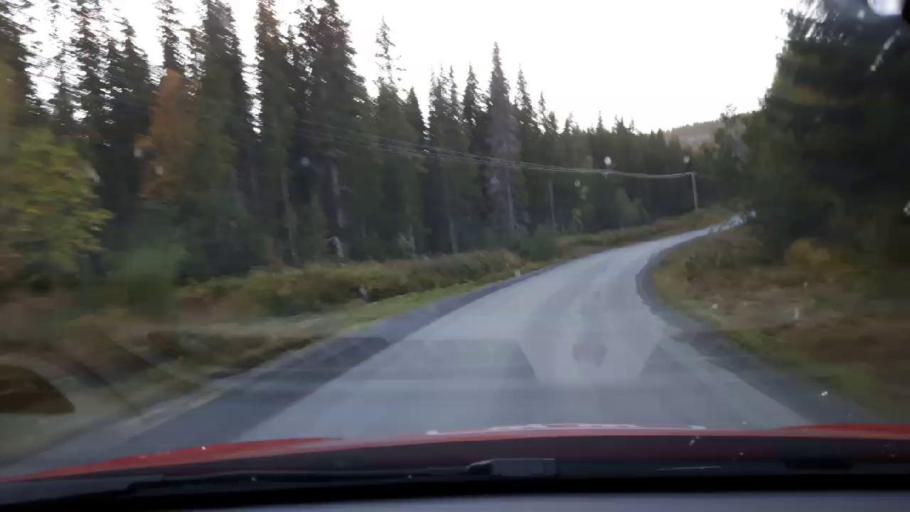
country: SE
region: Jaemtland
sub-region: Krokoms Kommun
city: Krokom
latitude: 63.4806
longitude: 14.2130
